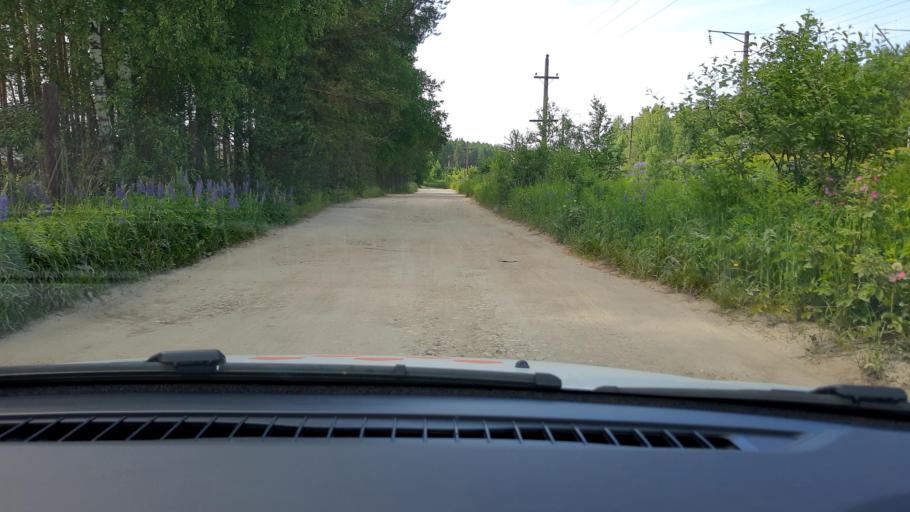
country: RU
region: Nizjnij Novgorod
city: Linda
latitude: 56.6639
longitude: 44.1686
